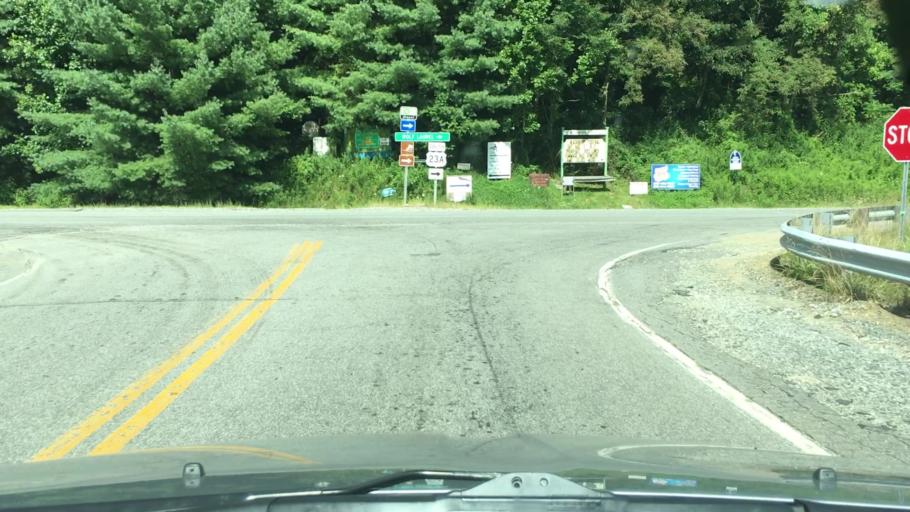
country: US
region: North Carolina
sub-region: Madison County
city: Mars Hill
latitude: 35.9099
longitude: -82.5556
